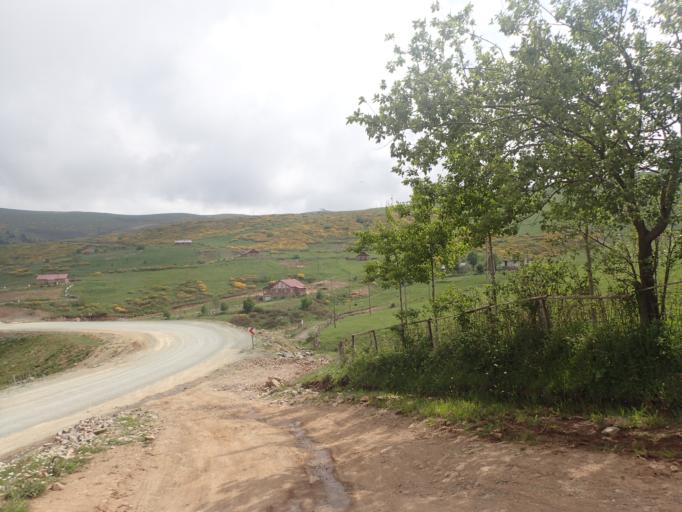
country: TR
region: Ordu
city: Topcam
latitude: 40.6419
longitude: 37.9376
